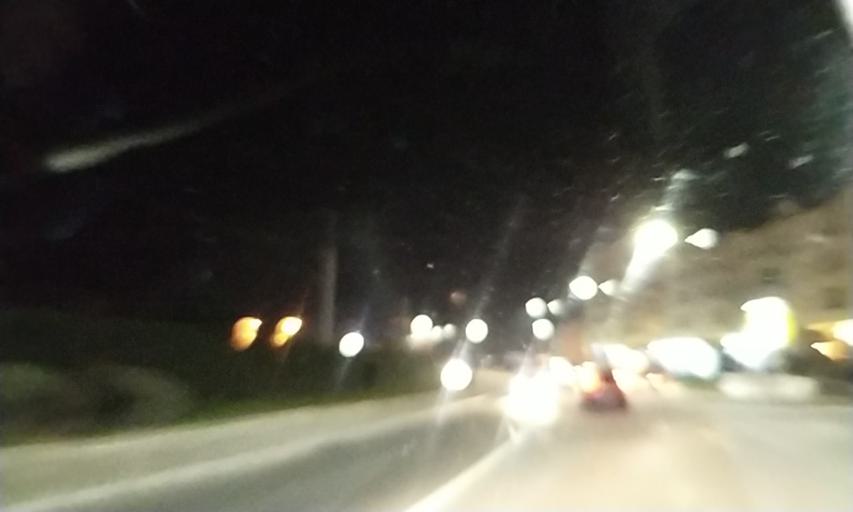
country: PT
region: Castelo Branco
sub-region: Concelho do Fundao
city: Fundao
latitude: 40.1462
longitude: -7.4994
